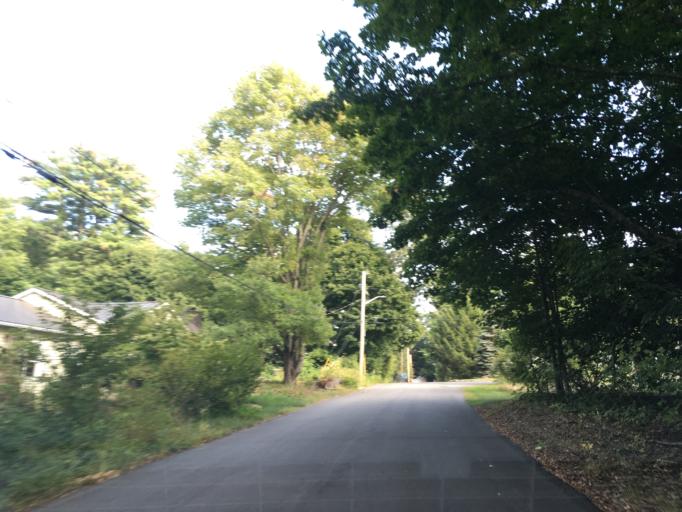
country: US
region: New Hampshire
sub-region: Rockingham County
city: Exeter
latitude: 42.9811
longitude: -70.9309
